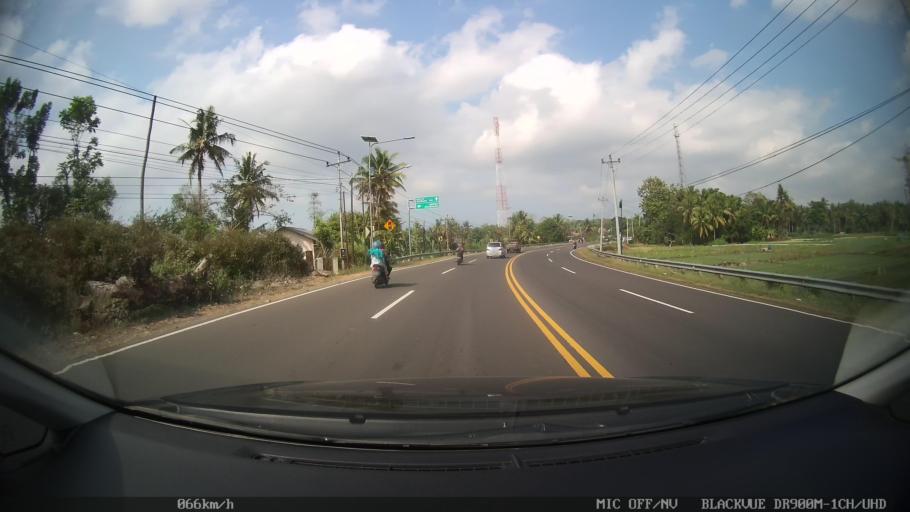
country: ID
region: Daerah Istimewa Yogyakarta
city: Srandakan
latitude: -7.8744
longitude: 110.2080
